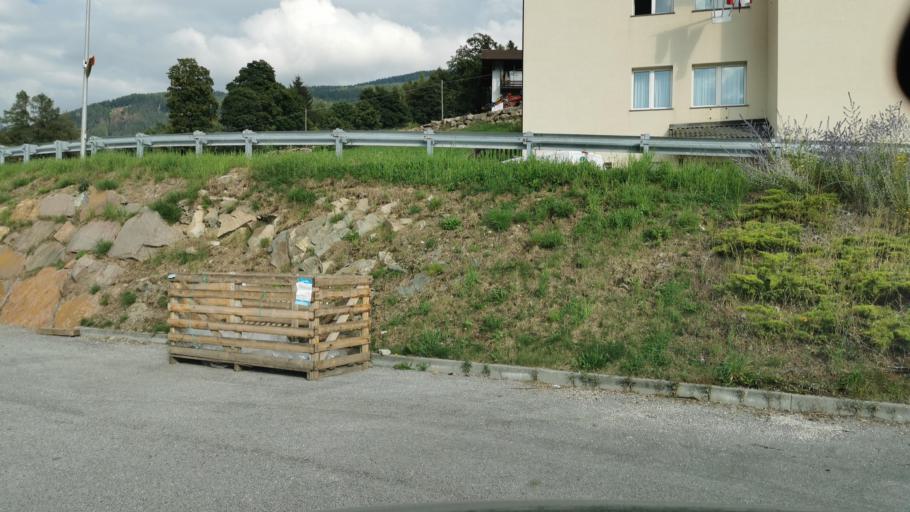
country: IT
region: Trentino-Alto Adige
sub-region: Provincia di Trento
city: Fierozzo
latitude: 46.1124
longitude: 11.3189
